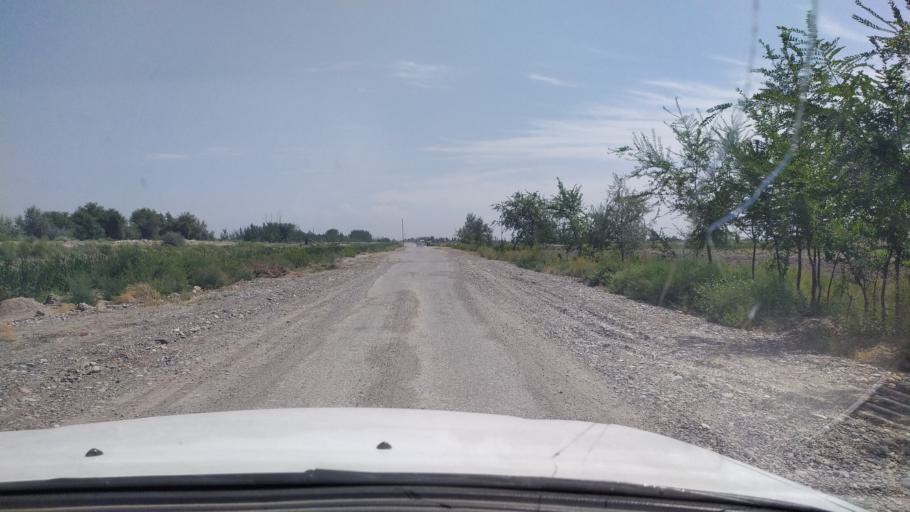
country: UZ
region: Namangan
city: Toshbuloq
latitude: 40.7949
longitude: 71.5810
